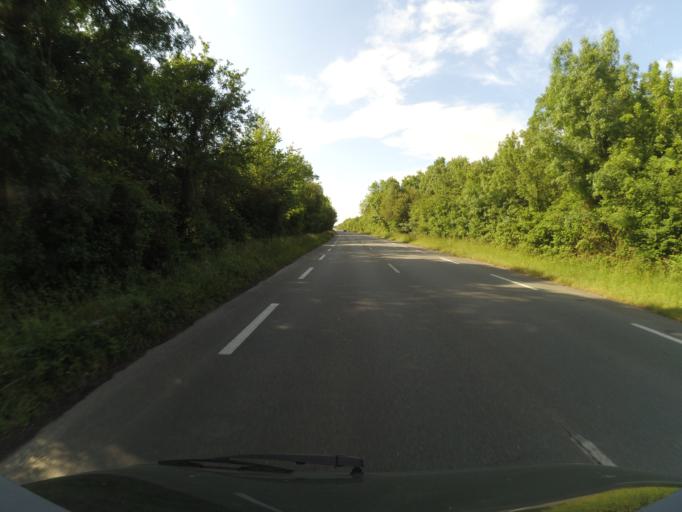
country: FR
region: Poitou-Charentes
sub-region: Departement de la Charente-Maritime
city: Saint-Agnant
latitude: 45.8232
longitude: -0.9327
